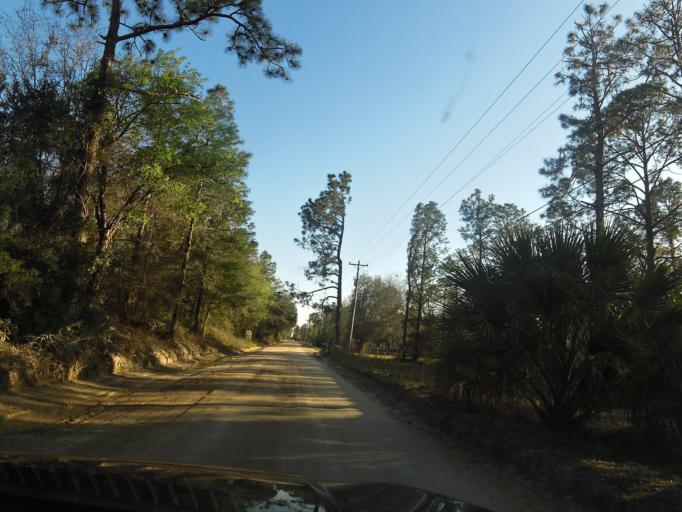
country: US
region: Florida
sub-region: Clay County
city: Middleburg
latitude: 30.1351
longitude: -81.8819
